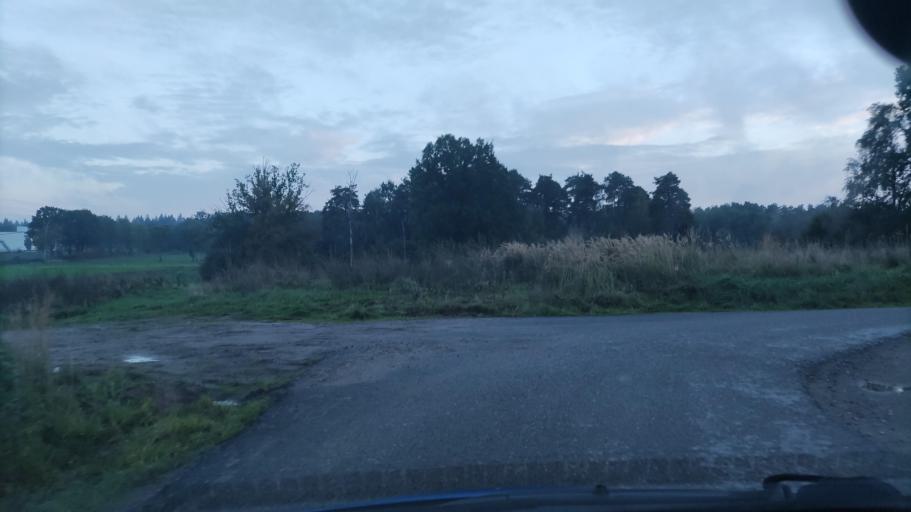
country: DE
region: Lower Saxony
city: Emmendorf
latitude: 52.9963
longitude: 10.5237
